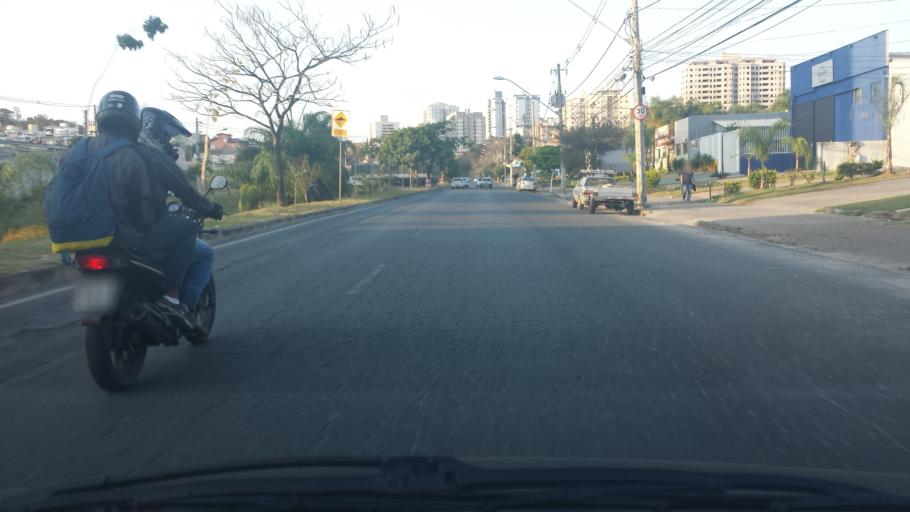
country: BR
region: Minas Gerais
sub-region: Belo Horizonte
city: Belo Horizonte
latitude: -19.8821
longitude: -43.9932
